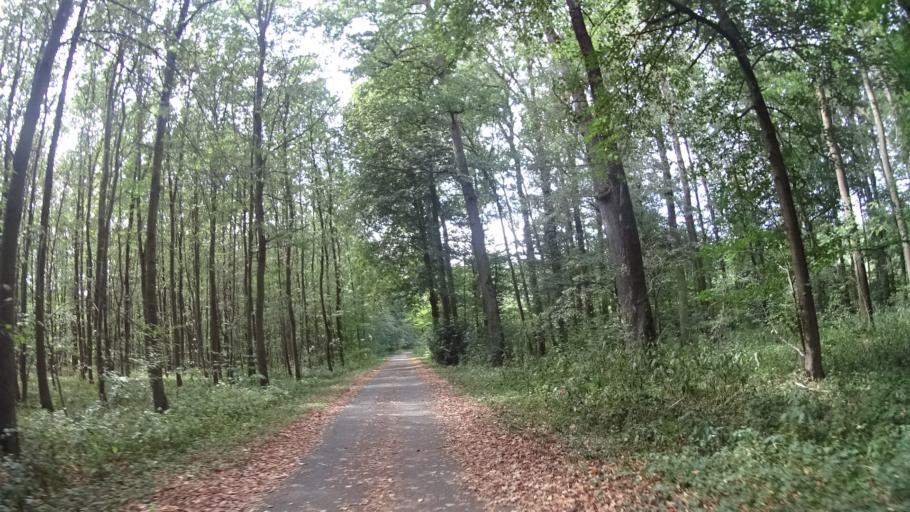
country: CZ
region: Olomoucky
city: Skrben
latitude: 49.6600
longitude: 17.1900
